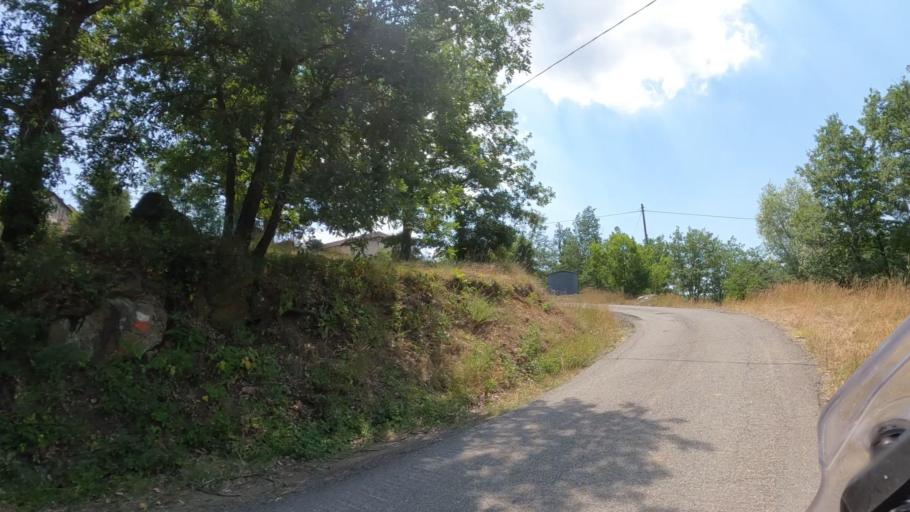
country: IT
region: Piedmont
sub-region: Provincia di Alessandria
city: Cassinelle-Concentrico
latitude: 44.5710
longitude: 8.5579
